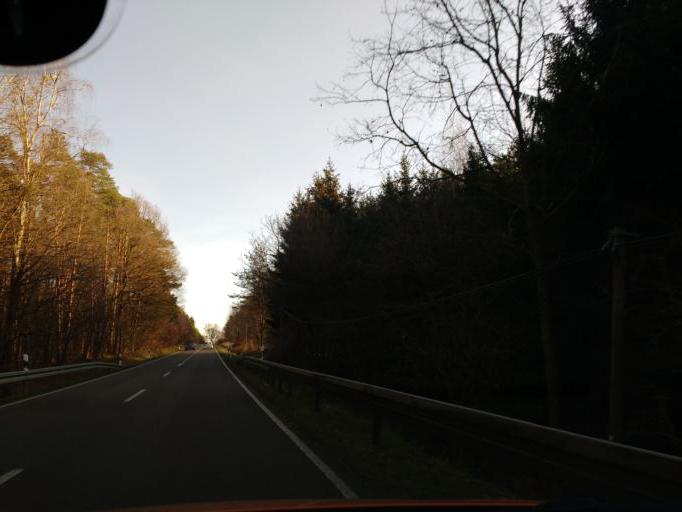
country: DE
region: Brandenburg
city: Protzel
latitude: 52.6443
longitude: 13.9537
